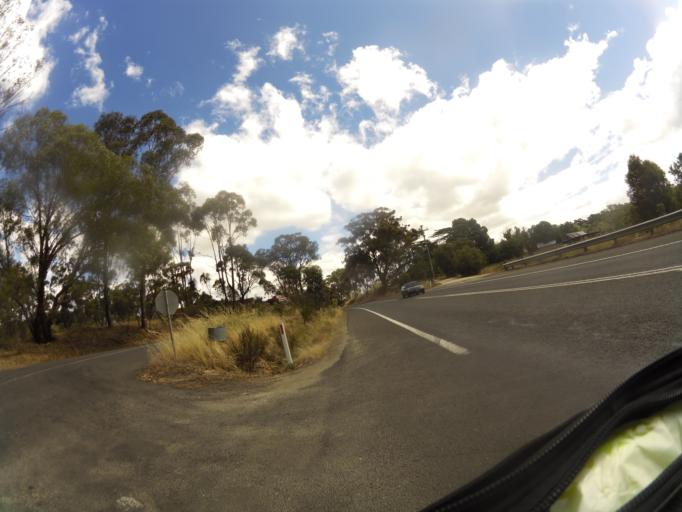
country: AU
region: Victoria
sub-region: Mount Alexander
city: Castlemaine
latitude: -37.0373
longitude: 144.2280
